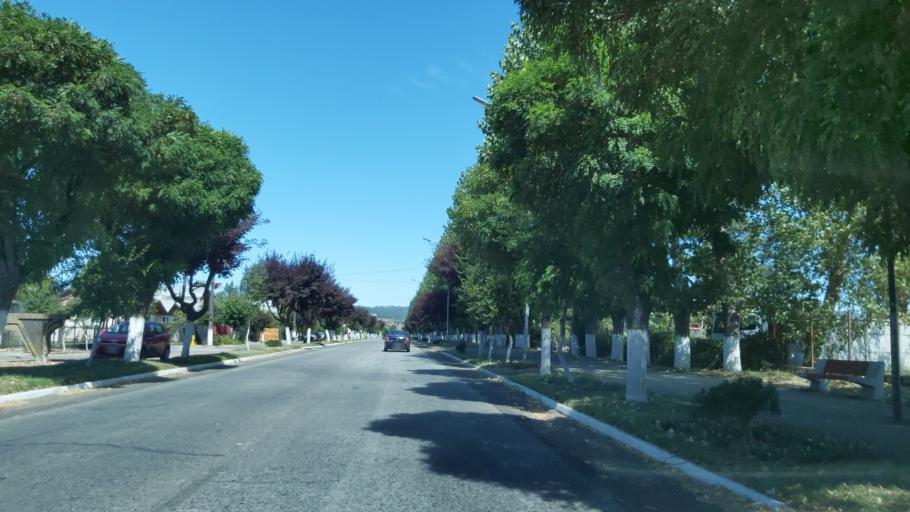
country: CL
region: Biobio
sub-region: Provincia de Concepcion
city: Lota
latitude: -37.1662
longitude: -72.9528
